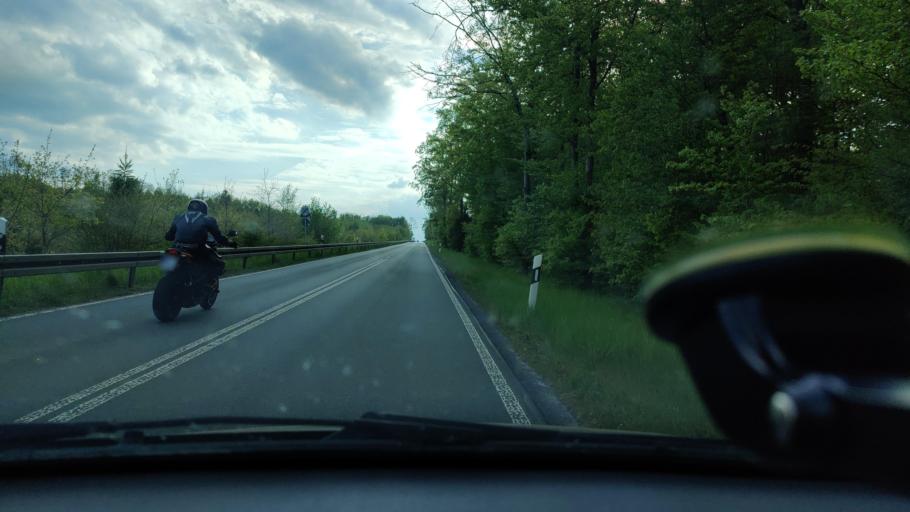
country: DE
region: North Rhine-Westphalia
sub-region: Regierungsbezirk Arnsberg
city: Brilon
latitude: 51.4482
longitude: 8.5964
